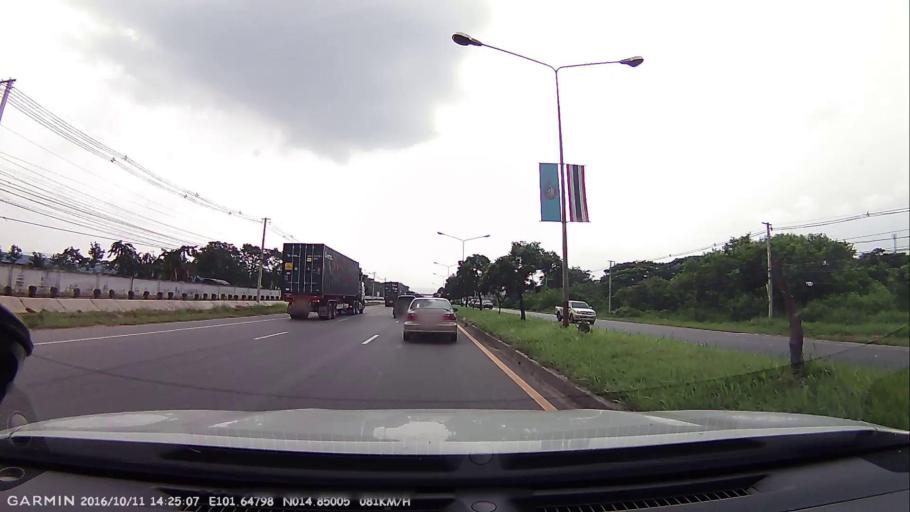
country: TH
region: Nakhon Ratchasima
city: Amphoe Sikhiu
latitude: 14.8501
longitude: 101.6480
